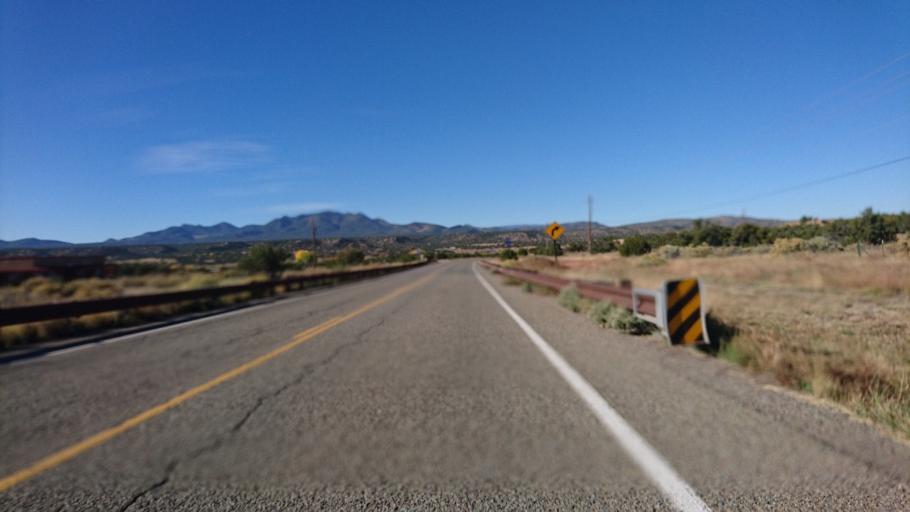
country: US
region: New Mexico
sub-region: Santa Fe County
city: La Cienega
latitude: 35.4315
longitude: -106.0874
